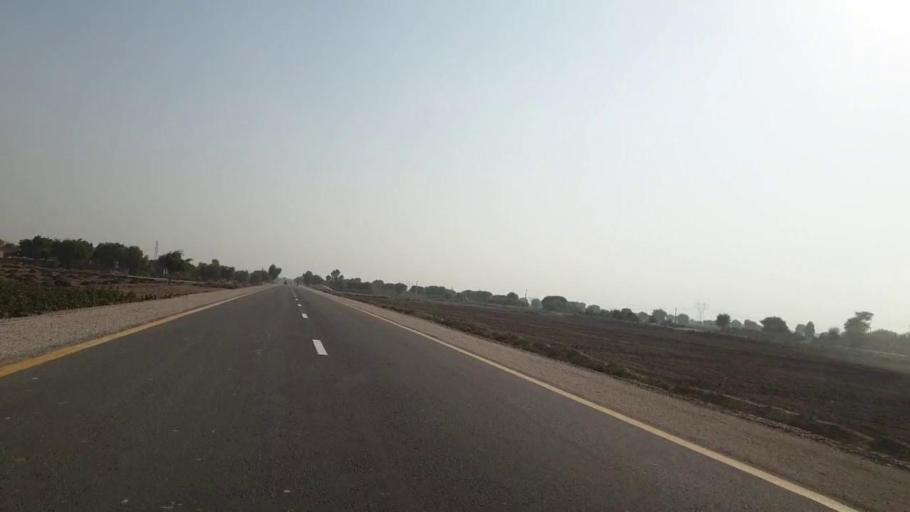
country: PK
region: Sindh
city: Bhan
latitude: 26.4916
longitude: 67.7799
